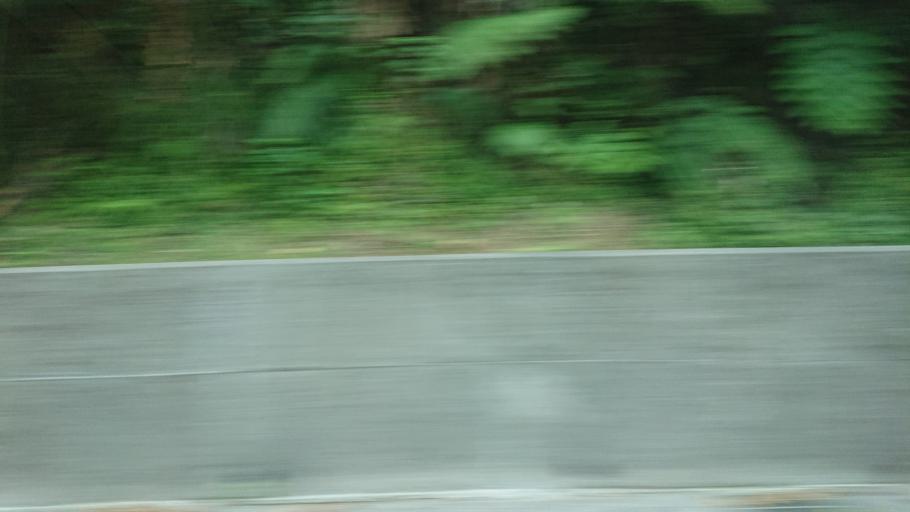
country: TW
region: Taiwan
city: Daxi
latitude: 24.8759
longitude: 121.3827
